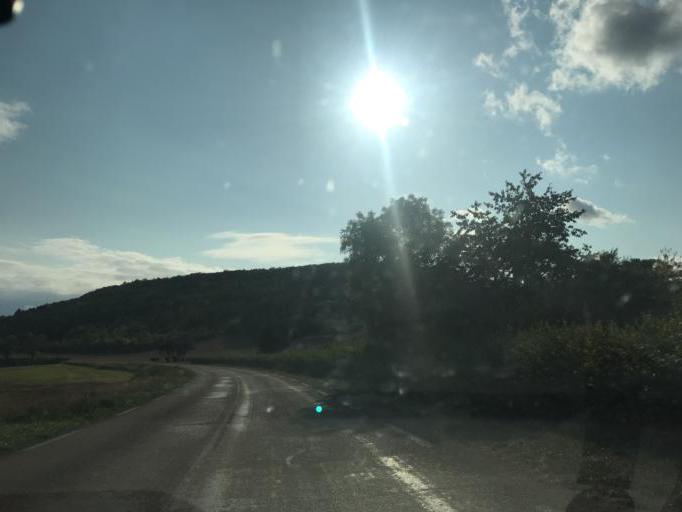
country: FR
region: Bourgogne
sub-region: Departement de l'Yonne
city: Joux-la-Ville
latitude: 47.5263
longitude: 3.7808
